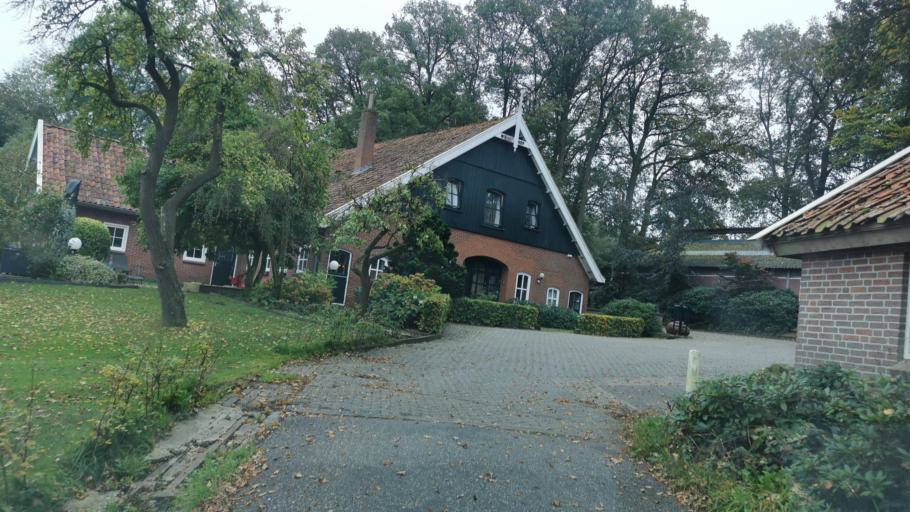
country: NL
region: Overijssel
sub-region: Gemeente Oldenzaal
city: Oldenzaal
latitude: 52.3237
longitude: 6.9453
